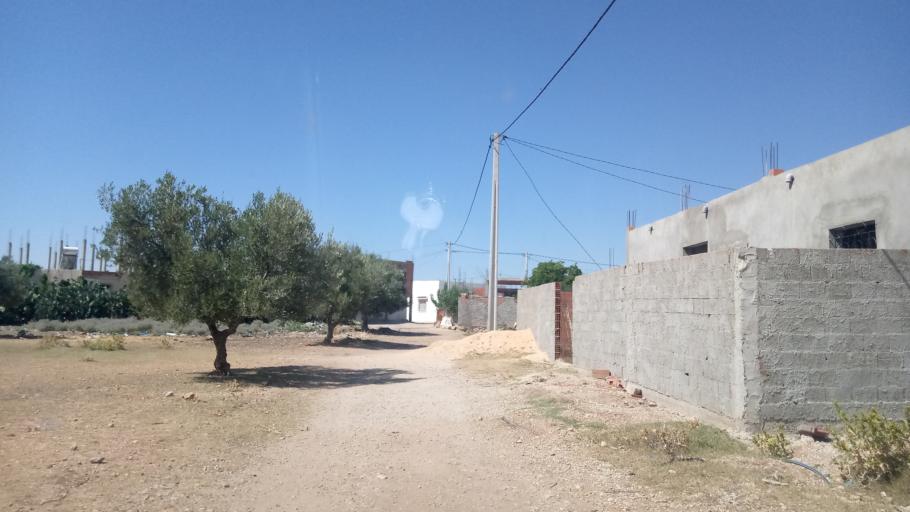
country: TN
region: Al Qayrawan
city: Sbikha
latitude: 36.1305
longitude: 10.0907
